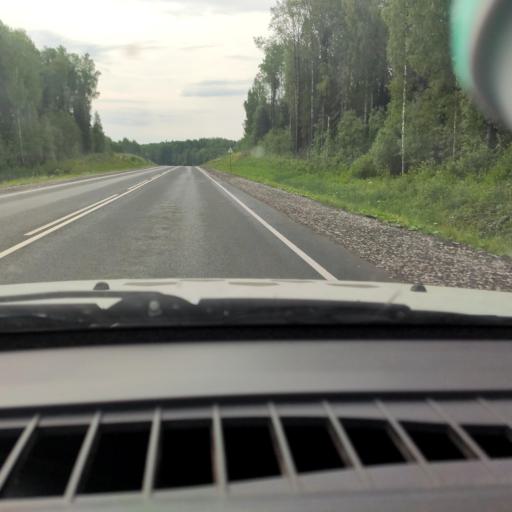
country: RU
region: Kirov
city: Kostino
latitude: 58.6581
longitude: 53.7696
